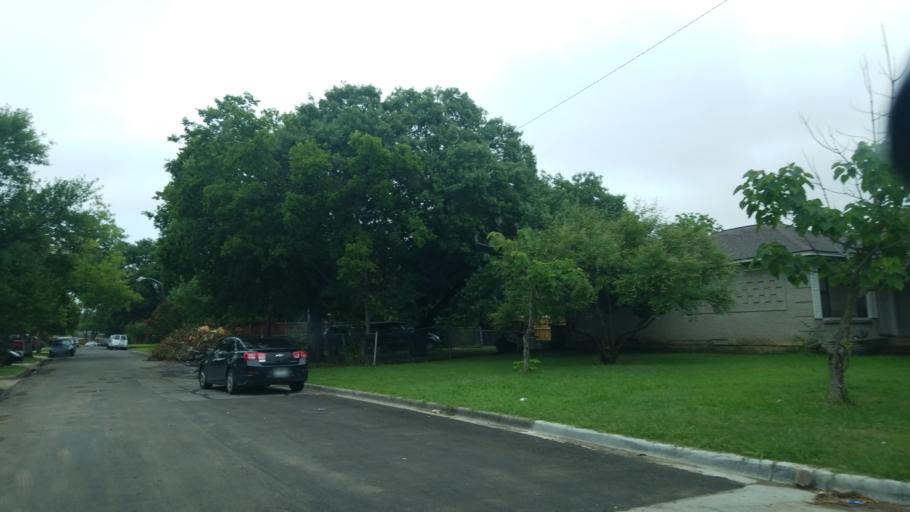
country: US
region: Texas
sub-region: Dallas County
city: Farmers Branch
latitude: 32.8942
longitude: -96.8807
